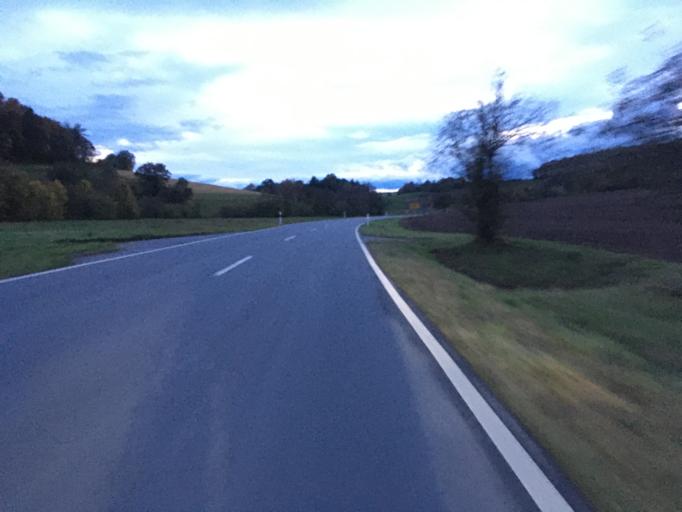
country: DE
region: Baden-Wuerttemberg
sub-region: Karlsruhe Region
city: Adelsheim
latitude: 49.3685
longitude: 9.4112
